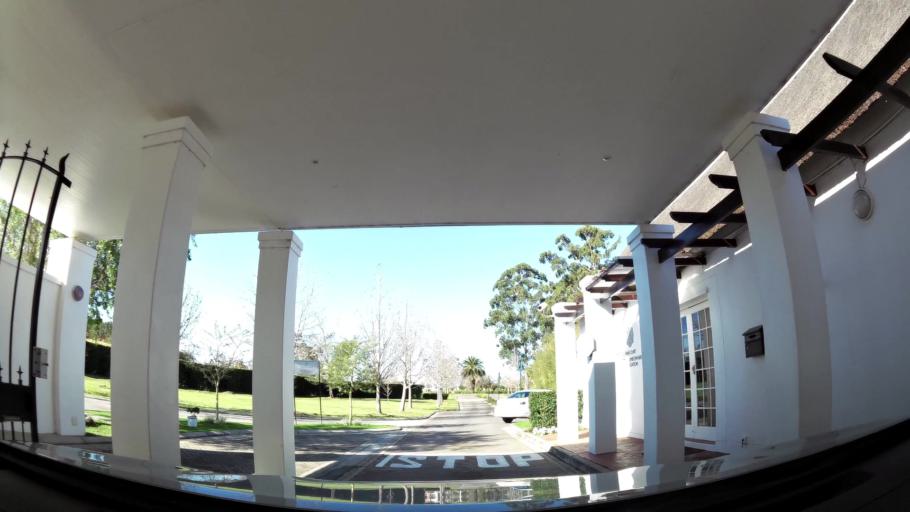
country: ZA
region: Western Cape
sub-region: Eden District Municipality
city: George
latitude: -33.9502
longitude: 22.4130
